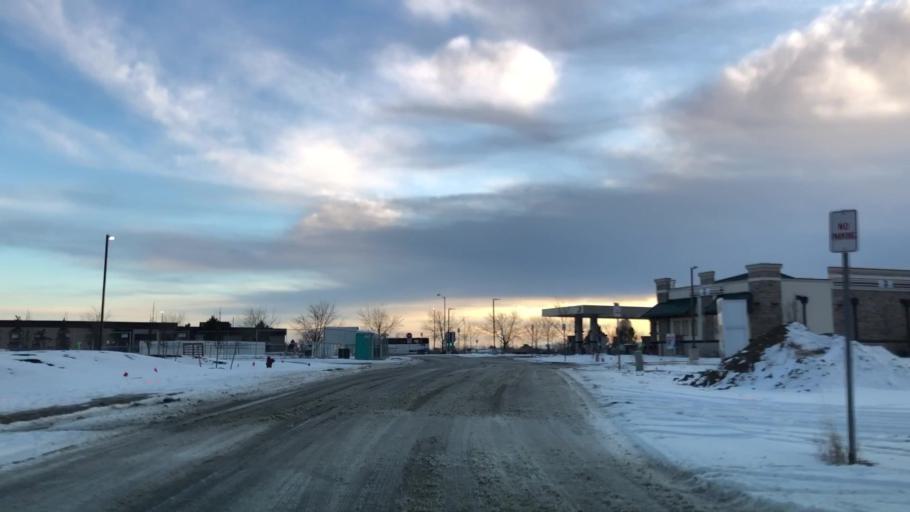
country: US
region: Colorado
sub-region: Weld County
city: Windsor
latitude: 40.4371
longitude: -104.9805
